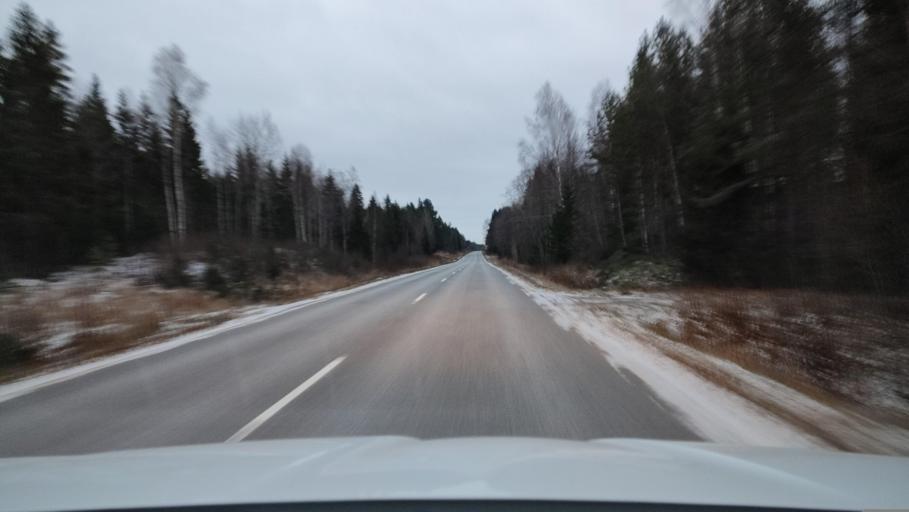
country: FI
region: Ostrobothnia
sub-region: Vaasa
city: Replot
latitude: 63.2535
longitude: 21.3707
